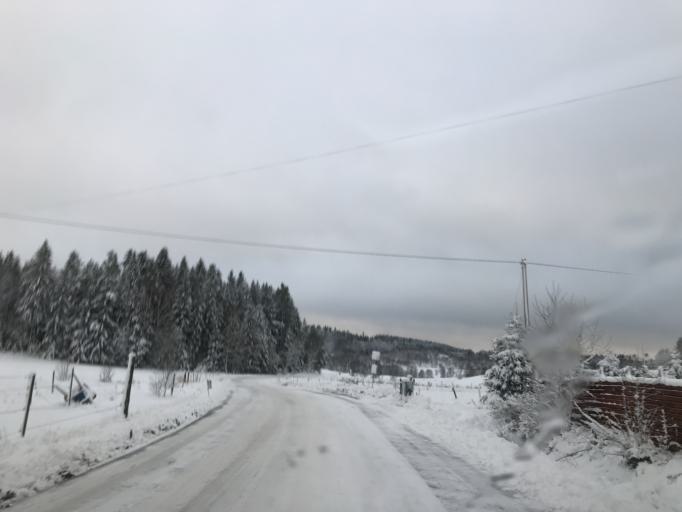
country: SE
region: Vaestra Goetaland
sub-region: Svenljunga Kommun
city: Svenljunga
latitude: 57.3939
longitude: 13.0702
